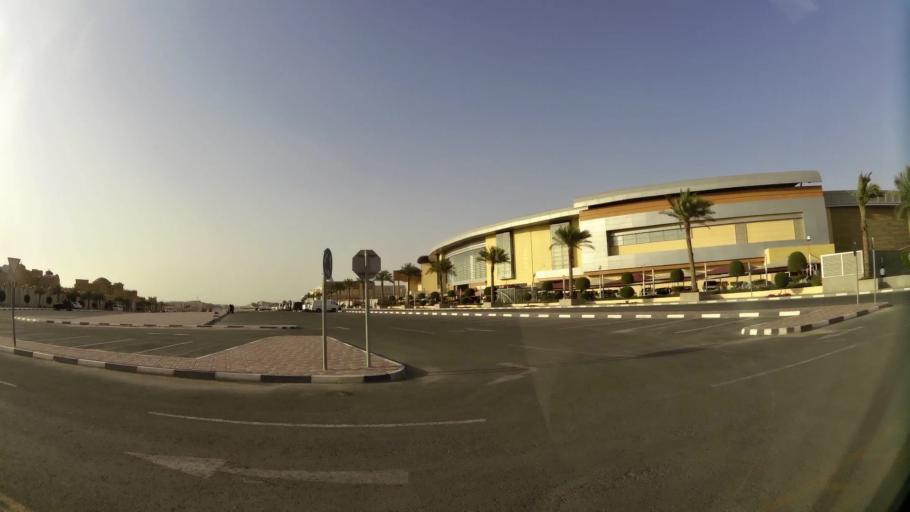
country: QA
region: Baladiyat ar Rayyan
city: Ar Rayyan
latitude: 25.3311
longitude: 51.4619
